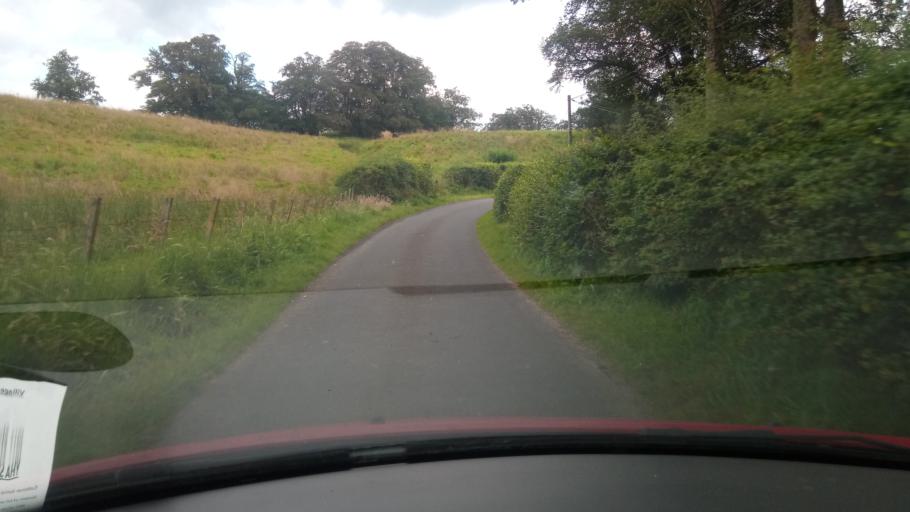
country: GB
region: Scotland
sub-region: The Scottish Borders
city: Jedburgh
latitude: 55.4119
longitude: -2.6241
